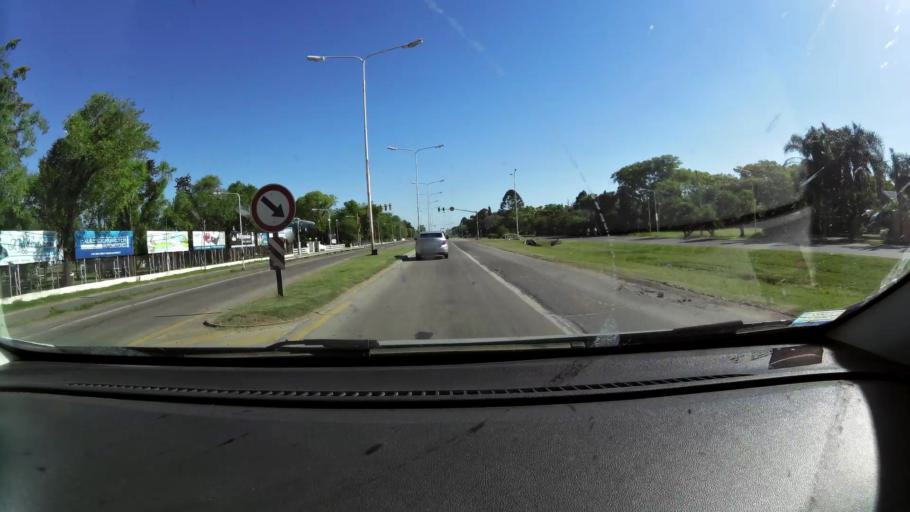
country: AR
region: Santa Fe
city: Rafaela
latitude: -31.2764
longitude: -61.5114
